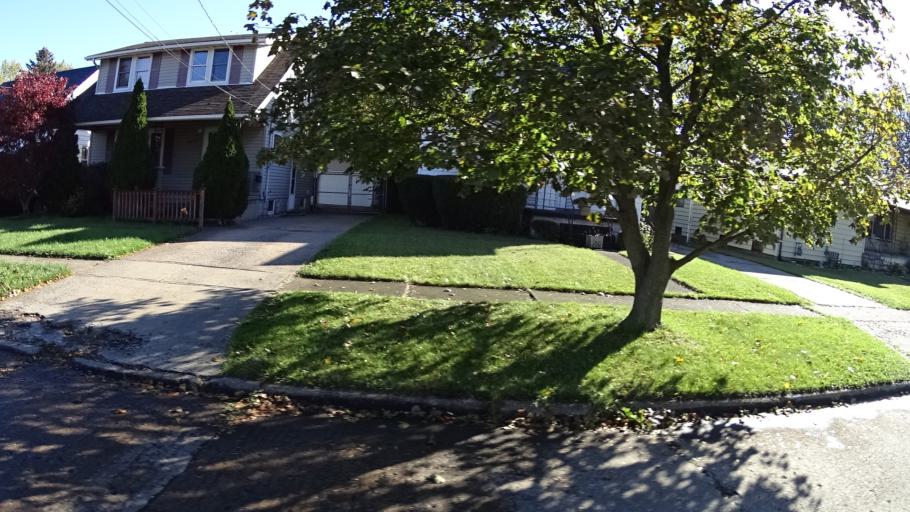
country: US
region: Ohio
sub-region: Lorain County
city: Lorain
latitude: 41.4427
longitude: -82.1604
